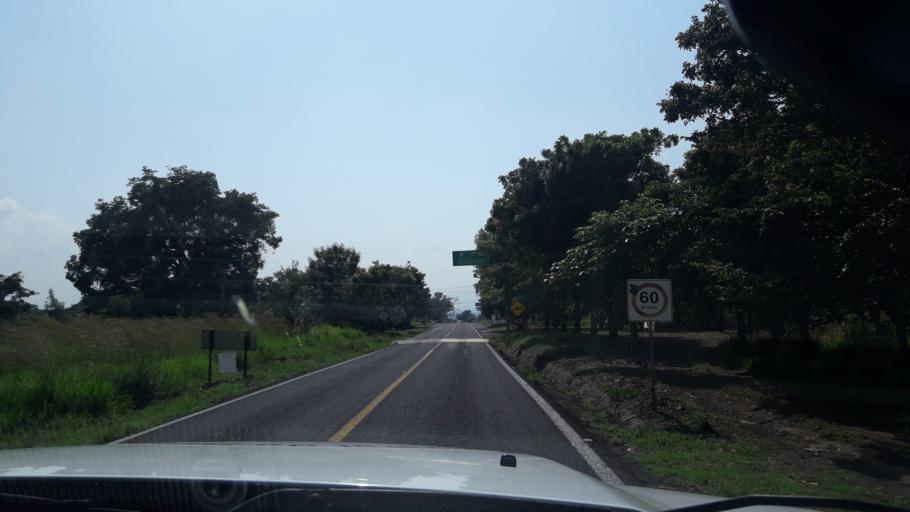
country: MX
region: Colima
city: Comala
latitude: 19.3462
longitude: -103.7394
